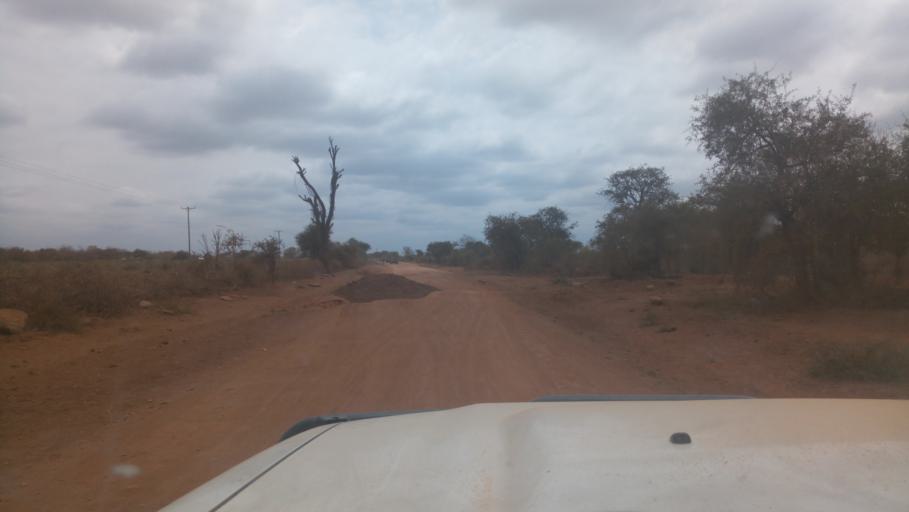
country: KE
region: Makueni
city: Wote
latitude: -1.8574
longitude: 37.9498
